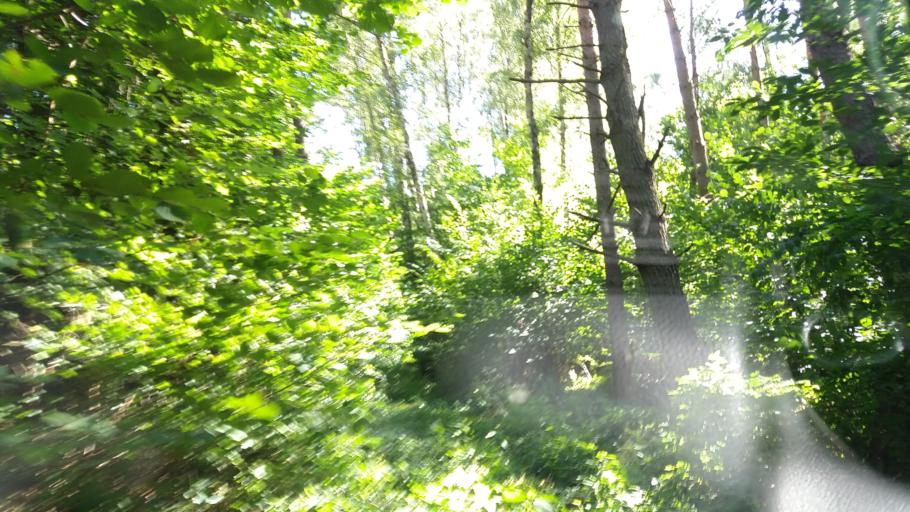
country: PL
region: West Pomeranian Voivodeship
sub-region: Powiat choszczenski
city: Krzecin
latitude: 53.0860
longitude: 15.4509
